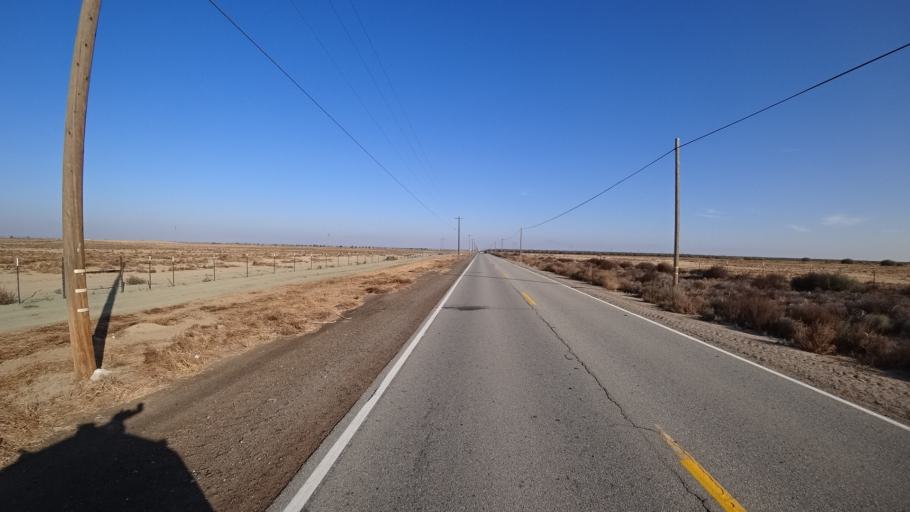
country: US
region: California
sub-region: Kern County
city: Rosedale
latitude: 35.2961
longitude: -119.1878
